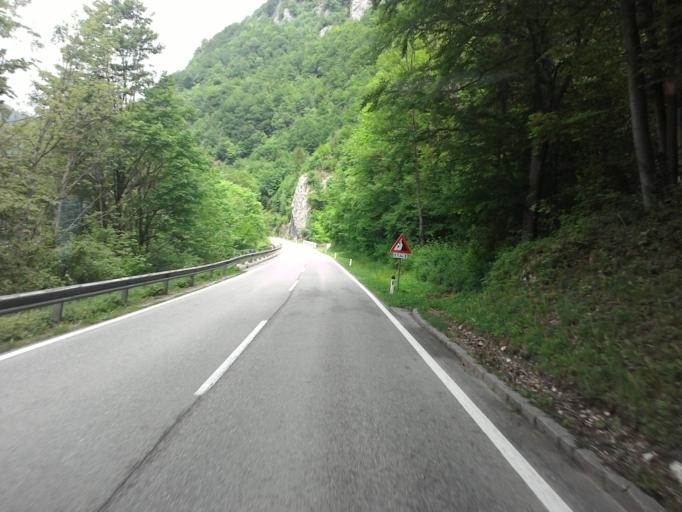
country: AT
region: Upper Austria
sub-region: Politischer Bezirk Steyr-Land
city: Weyer
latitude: 47.8685
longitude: 14.6099
